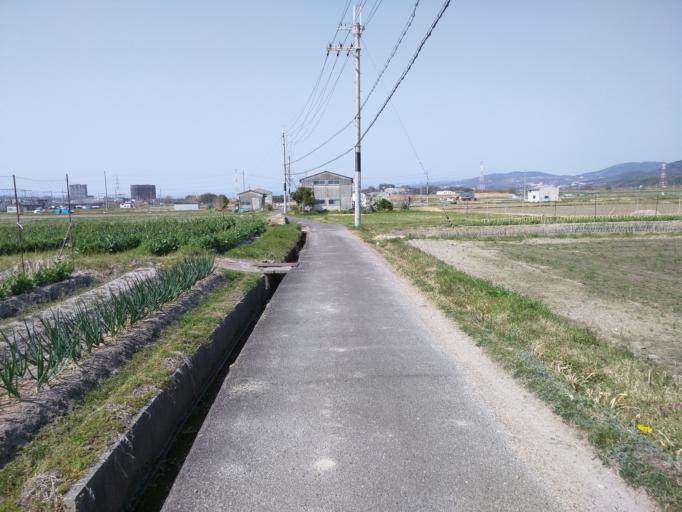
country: JP
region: Kyoto
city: Tanabe
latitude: 34.7859
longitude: 135.7903
